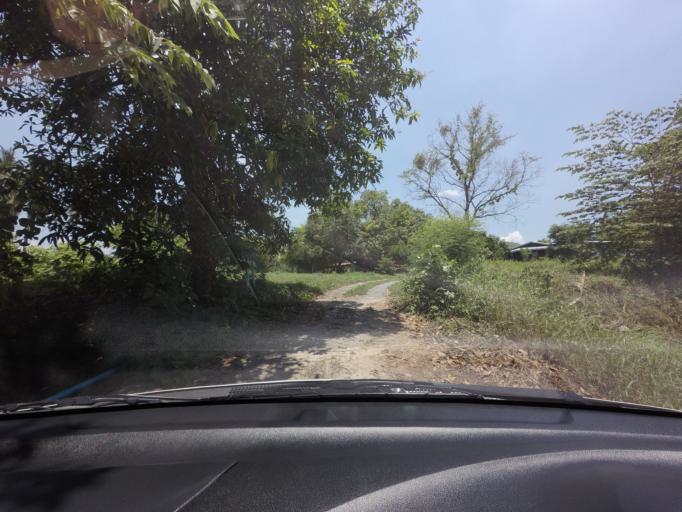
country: TH
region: Suphan Buri
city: Dan Chang
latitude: 14.9105
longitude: 99.7055
